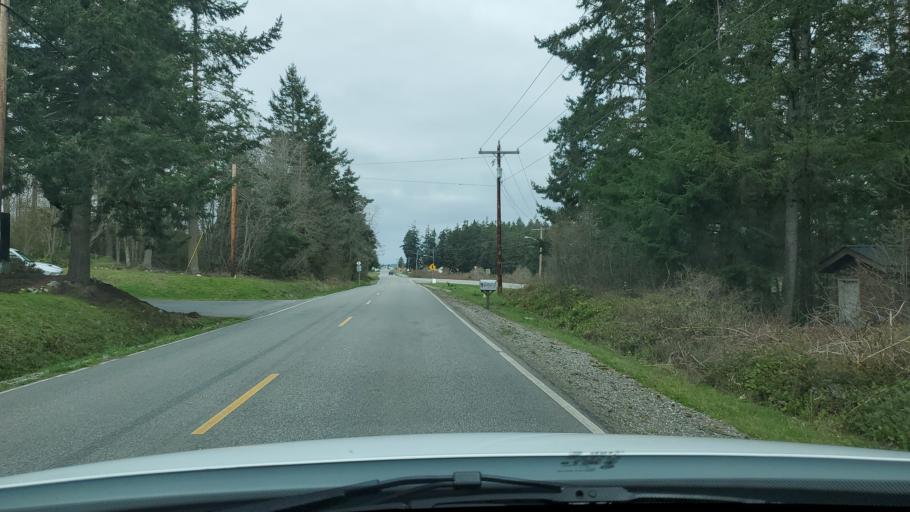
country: US
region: Washington
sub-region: Island County
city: Oak Harbor
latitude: 48.3124
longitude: -122.6307
